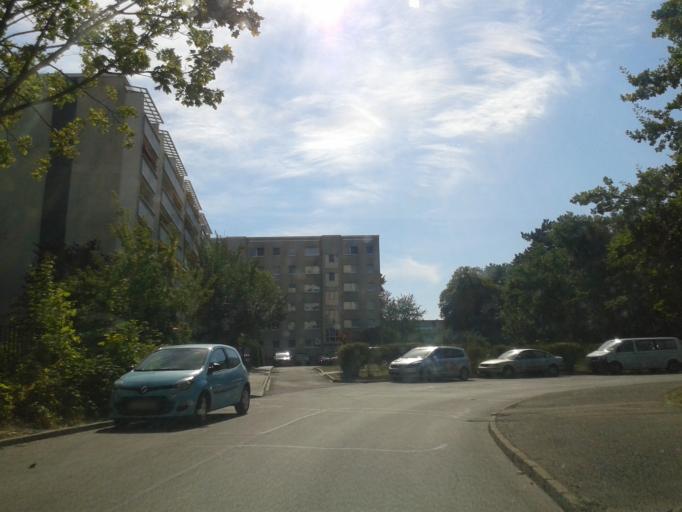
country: DE
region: Saxony
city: Dresden
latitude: 51.0331
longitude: 13.7874
